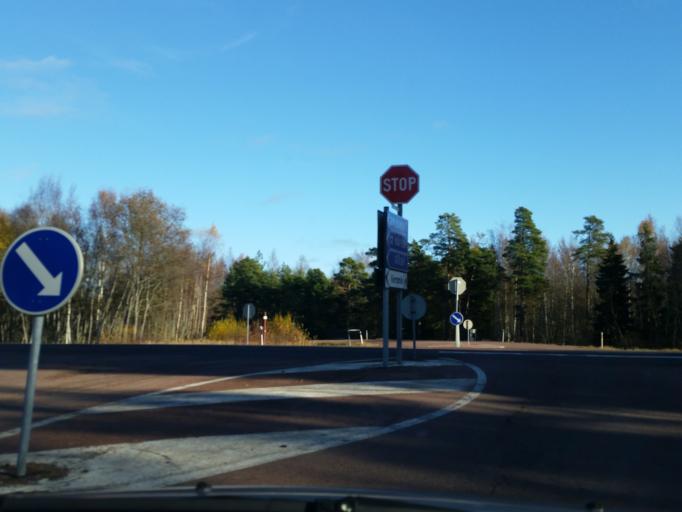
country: AX
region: Alands landsbygd
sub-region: Jomala
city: Jomala
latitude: 60.1977
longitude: 19.9510
